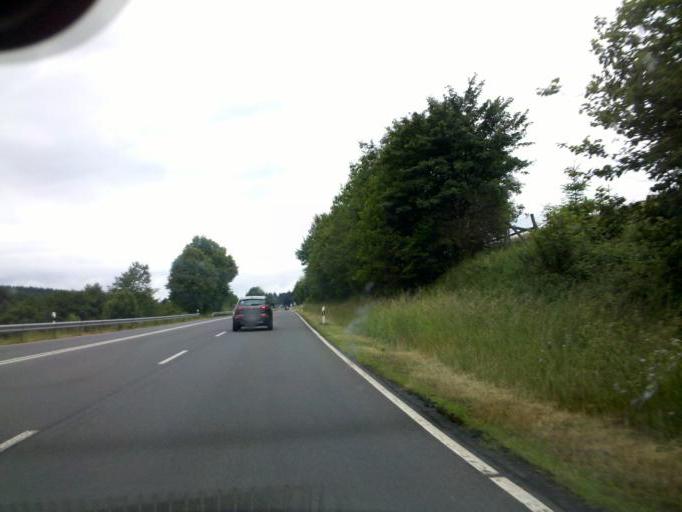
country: DE
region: North Rhine-Westphalia
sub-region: Regierungsbezirk Arnsberg
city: Attendorn
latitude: 51.0705
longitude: 7.9382
